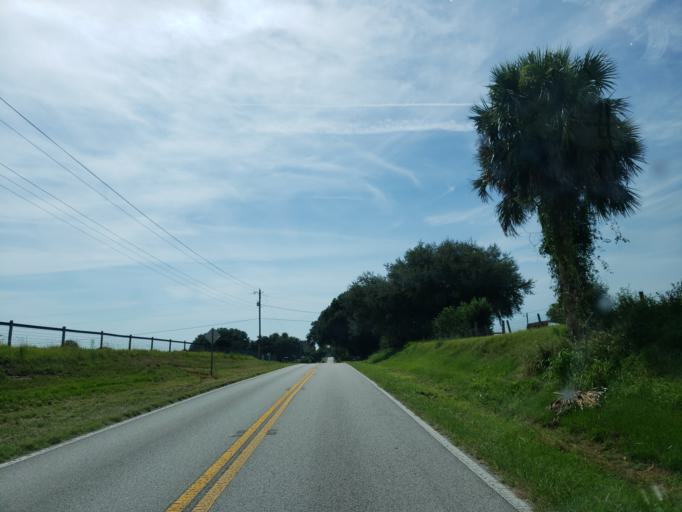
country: US
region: Florida
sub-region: Pasco County
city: San Antonio
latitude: 28.3907
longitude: -82.2931
